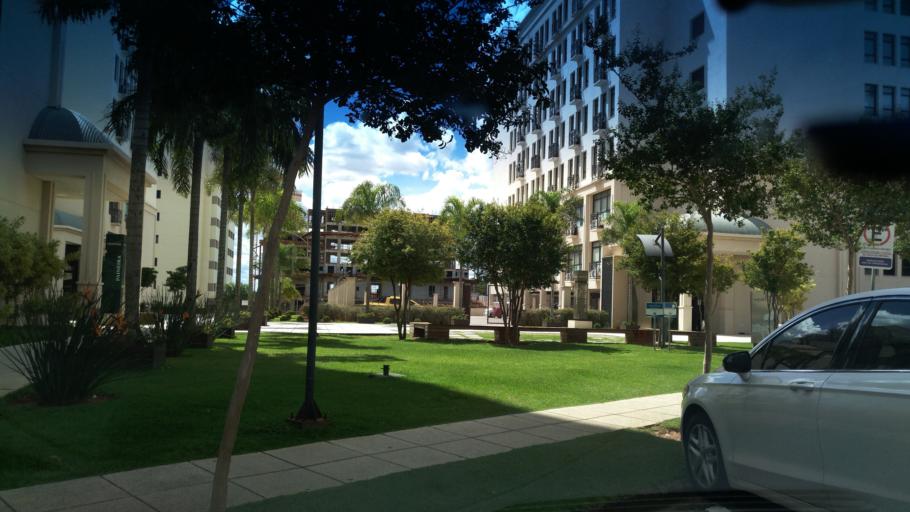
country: BR
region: Sao Paulo
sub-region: Valinhos
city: Valinhos
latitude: -22.9810
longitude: -47.0124
